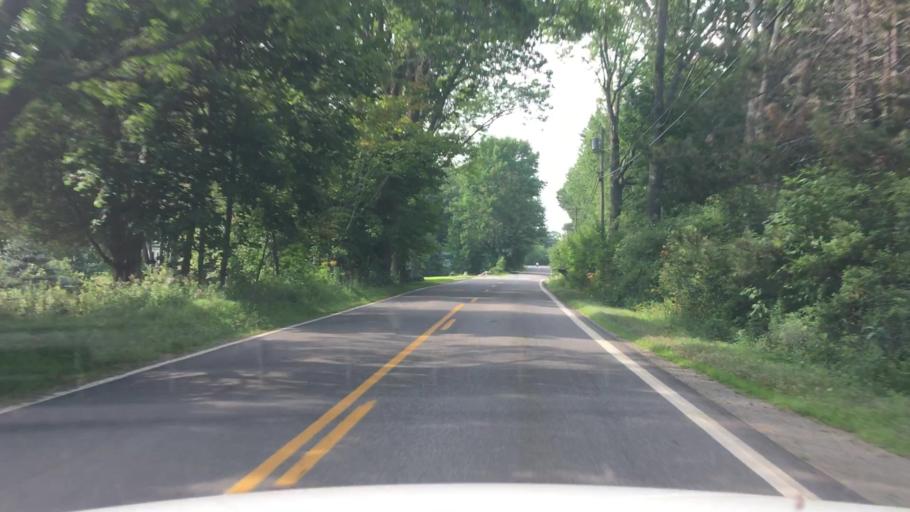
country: US
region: Maine
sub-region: Lincoln County
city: Waldoboro
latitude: 44.1578
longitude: -69.3764
